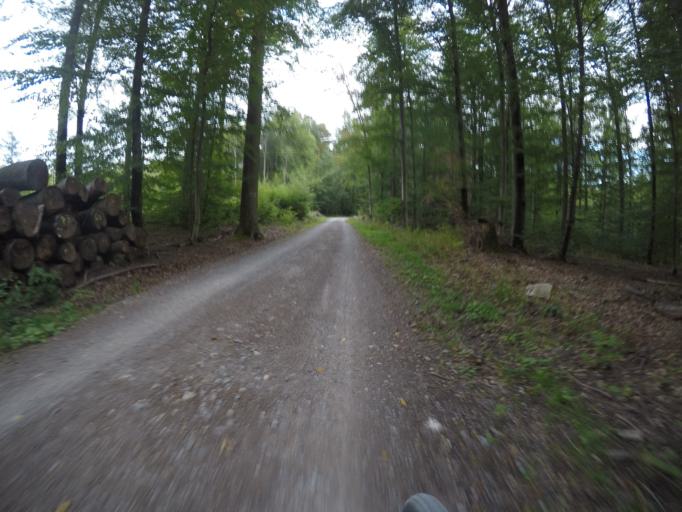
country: DE
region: Baden-Wuerttemberg
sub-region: Regierungsbezirk Stuttgart
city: Gerlingen
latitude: 48.7513
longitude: 9.0564
